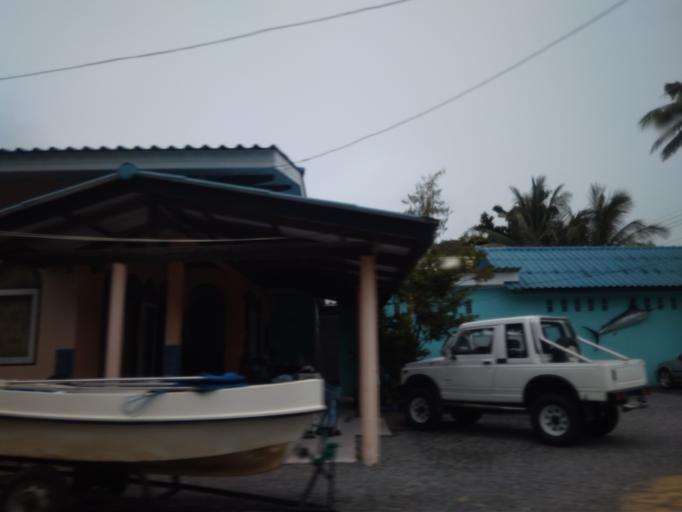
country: TH
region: Phuket
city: Mueang Phuket
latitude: 7.8145
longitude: 98.3958
